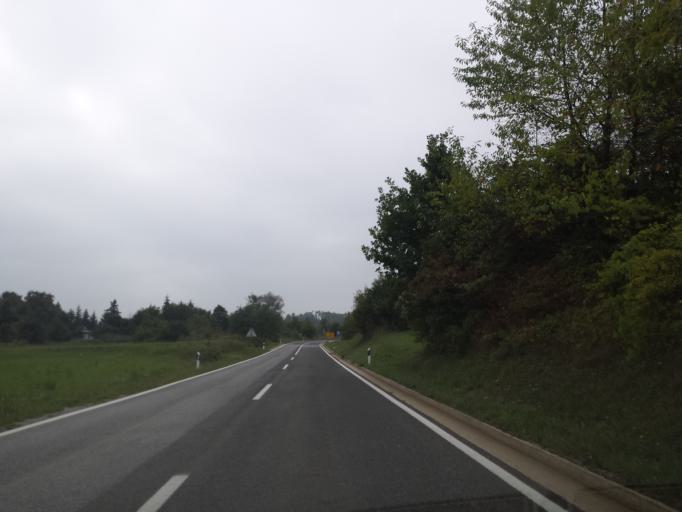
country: HR
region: Karlovacka
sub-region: Grad Karlovac
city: Karlovac
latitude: 45.4228
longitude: 15.4747
